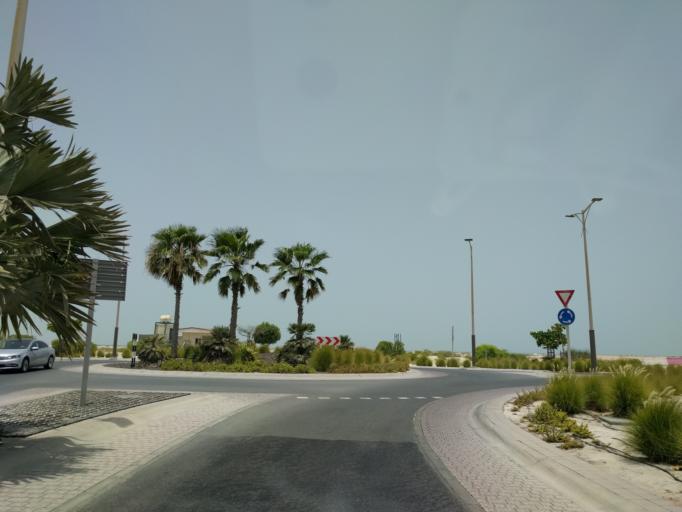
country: AE
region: Abu Dhabi
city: Abu Dhabi
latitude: 24.5536
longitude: 54.4488
